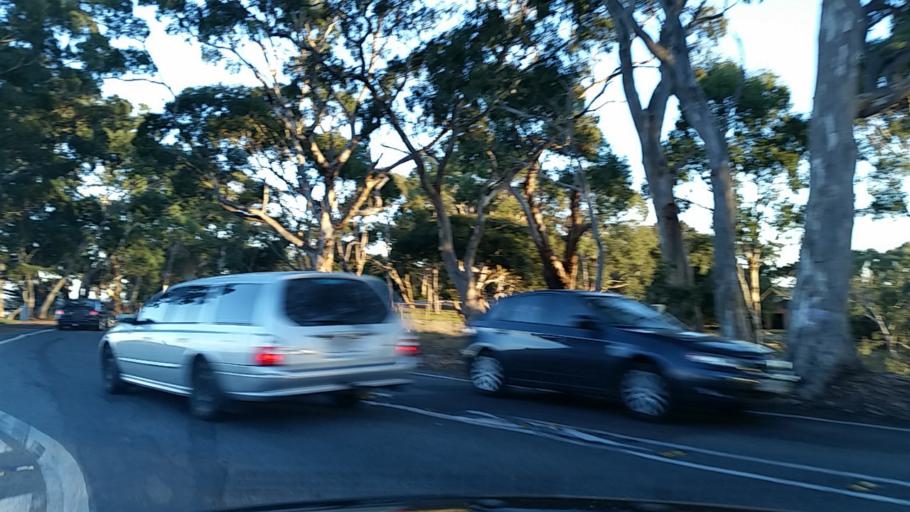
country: AU
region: South Australia
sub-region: Onkaparinga
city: Craigburn Farm
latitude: -35.0722
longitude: 138.6276
